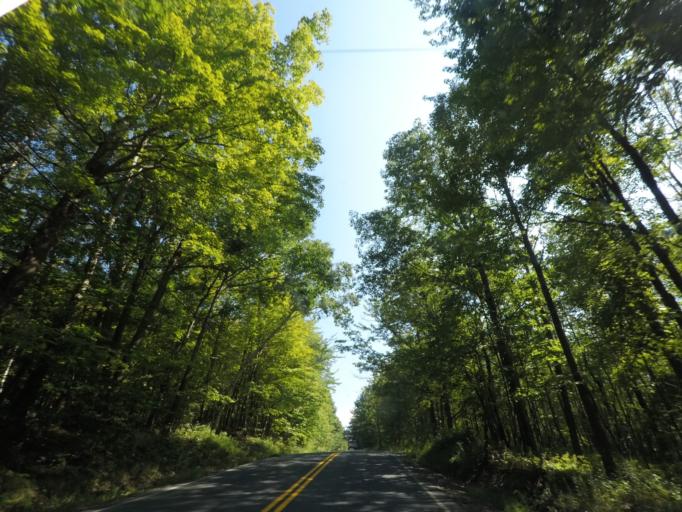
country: US
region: New York
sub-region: Rensselaer County
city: Poestenkill
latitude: 42.7367
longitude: -73.5112
